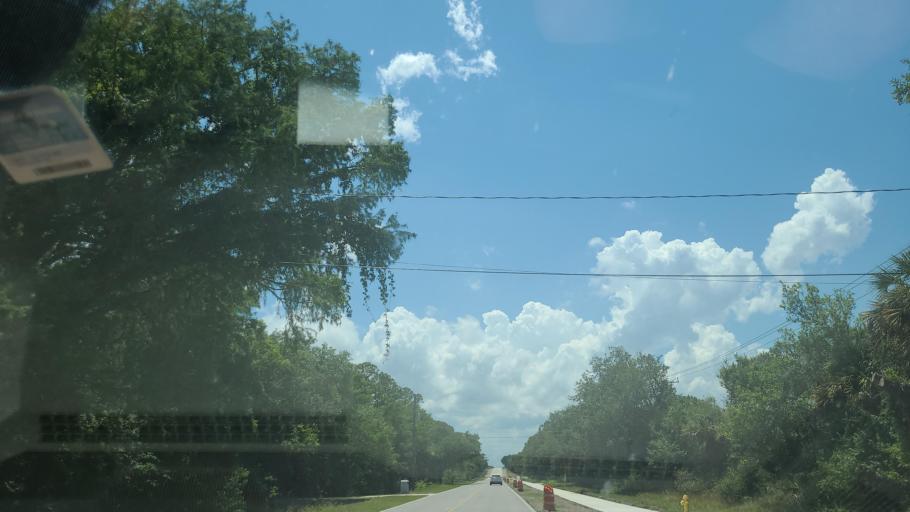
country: US
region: Florida
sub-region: Brevard County
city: Grant-Valkaria
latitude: 27.9537
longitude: -80.6028
